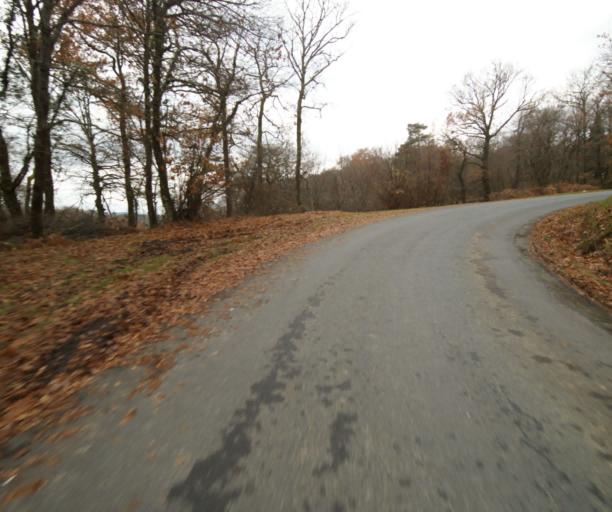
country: FR
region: Limousin
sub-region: Departement de la Correze
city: Chameyrat
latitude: 45.2392
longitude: 1.7290
